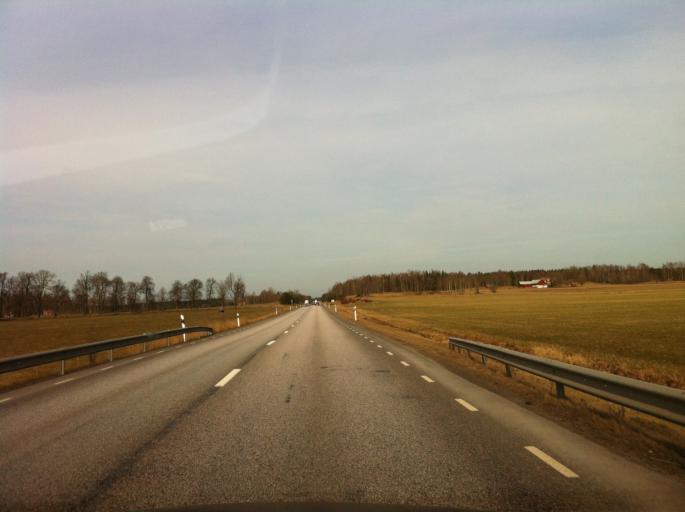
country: SE
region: Vaestra Goetaland
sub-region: Mariestads Kommun
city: Mariestad
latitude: 58.7956
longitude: 13.9686
